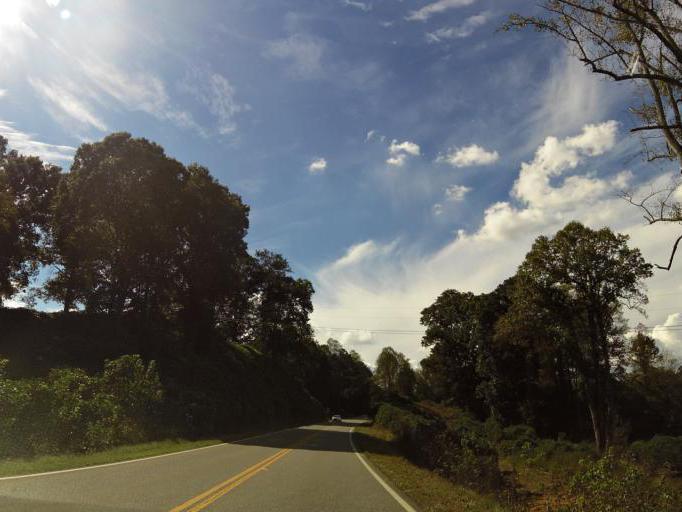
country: US
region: Georgia
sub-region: Pickens County
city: Nelson
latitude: 34.4103
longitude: -84.4004
